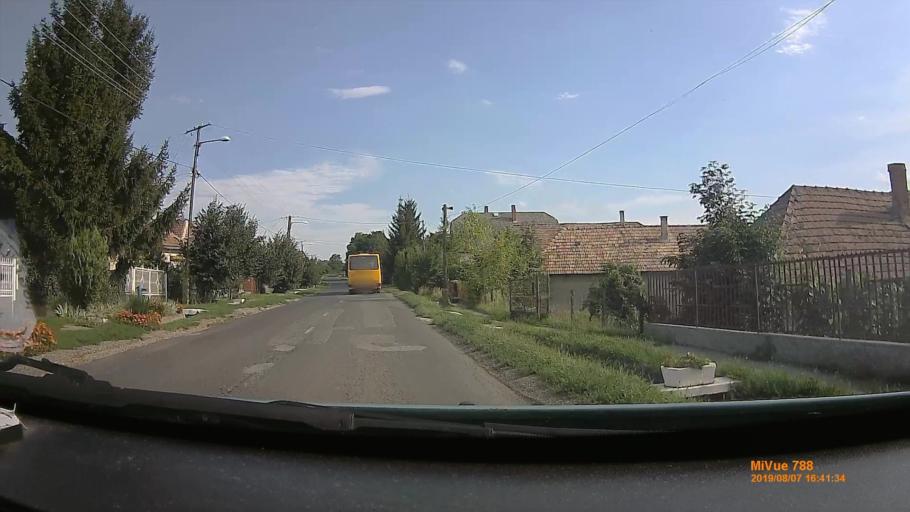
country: HU
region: Borsod-Abauj-Zemplen
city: Encs
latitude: 48.3772
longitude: 21.2138
